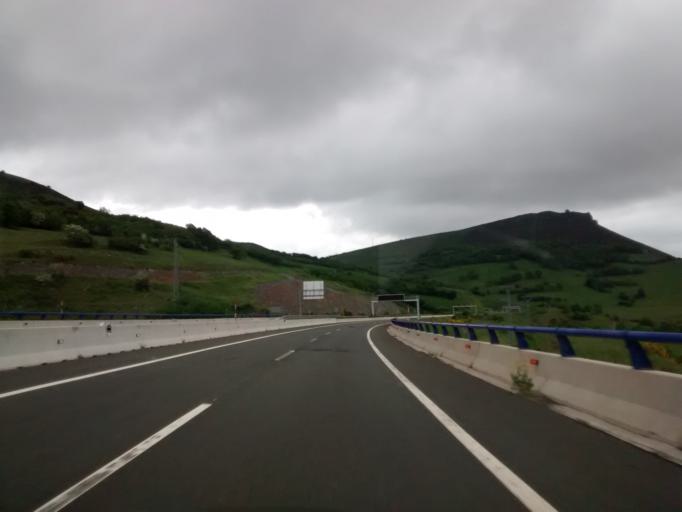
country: ES
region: Cantabria
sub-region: Provincia de Cantabria
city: Pesquera
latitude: 43.0806
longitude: -4.0855
